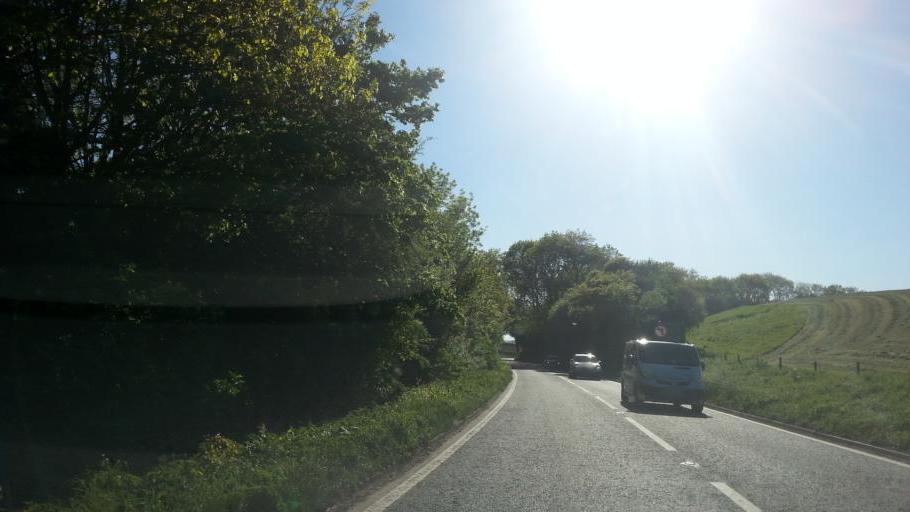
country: GB
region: England
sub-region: Somerset
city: Castle Cary
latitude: 51.0655
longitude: -2.4766
